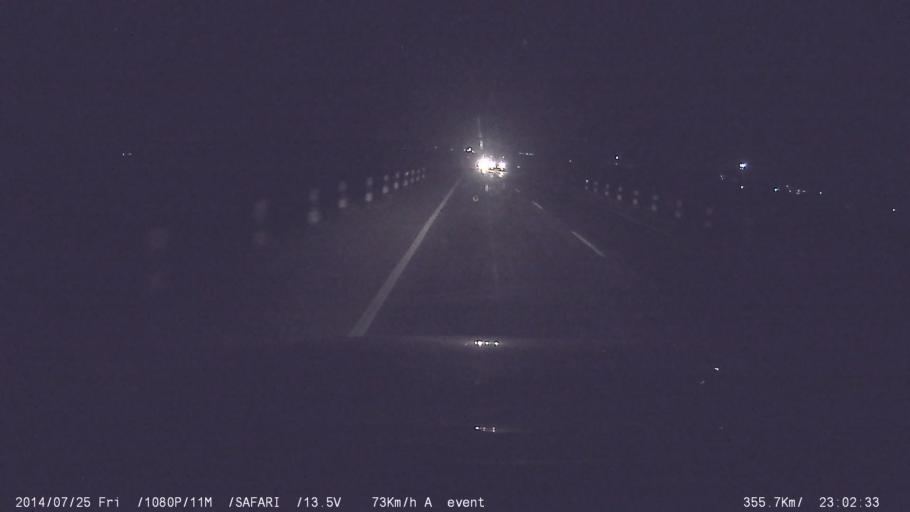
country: IN
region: Tamil Nadu
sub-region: Coimbatore
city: Chettipalaiyam
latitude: 10.9370
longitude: 77.0047
